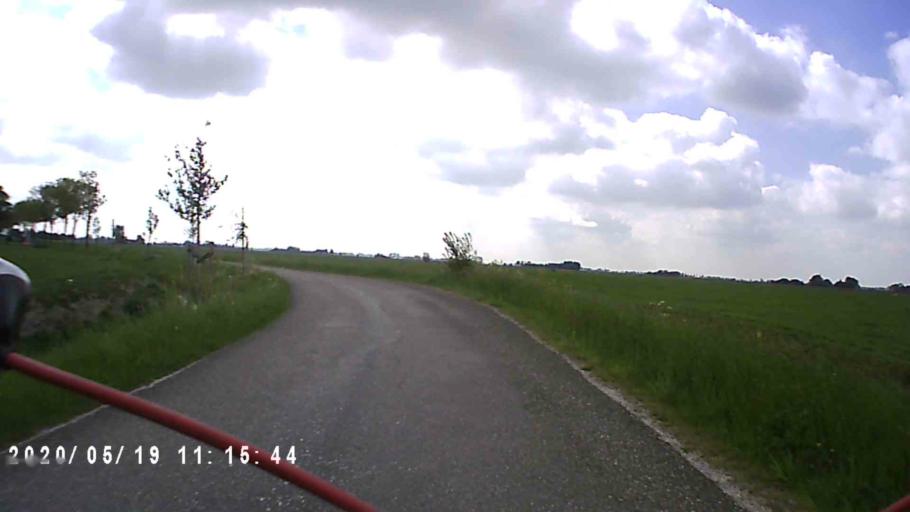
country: NL
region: Groningen
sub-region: Gemeente Zuidhorn
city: Oldehove
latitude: 53.2920
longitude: 6.3568
